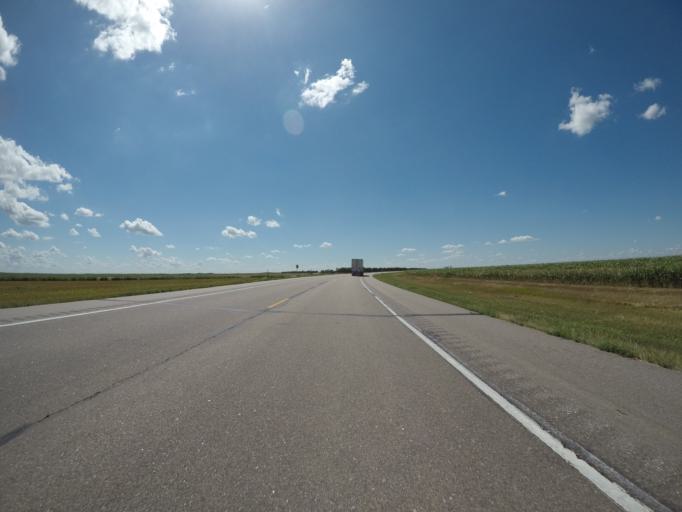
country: US
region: Nebraska
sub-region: Chase County
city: Imperial
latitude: 40.4942
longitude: -101.5943
